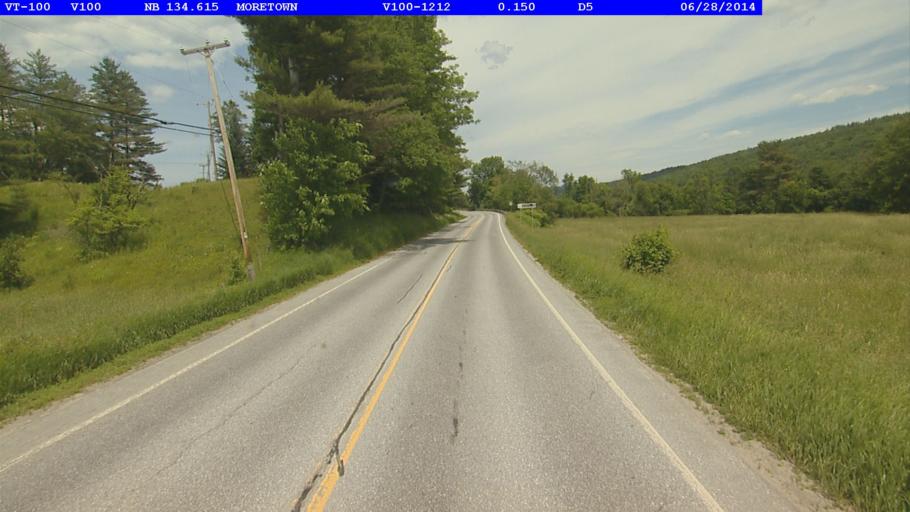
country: US
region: Vermont
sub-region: Washington County
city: Waterbury
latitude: 44.2366
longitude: -72.7782
